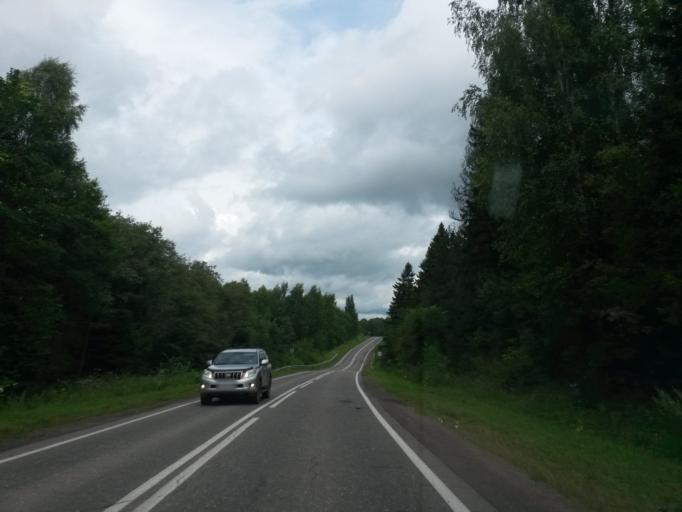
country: RU
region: Jaroslavl
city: Yaroslavl
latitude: 57.7953
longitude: 39.8281
